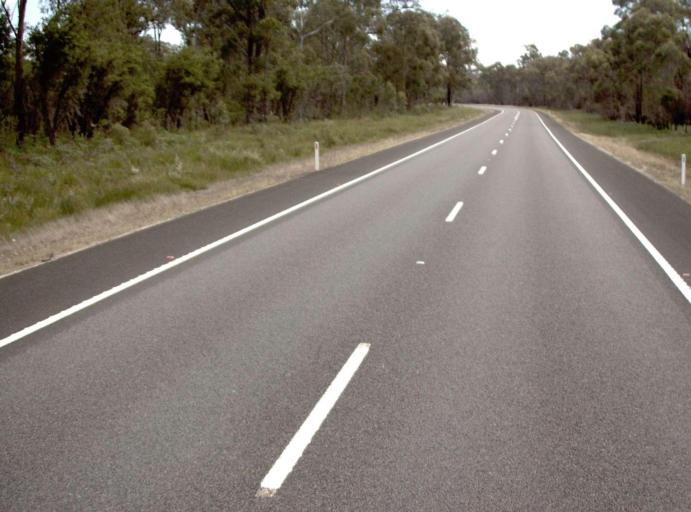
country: AU
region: New South Wales
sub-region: Bega Valley
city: Eden
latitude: -37.5158
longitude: 149.5010
